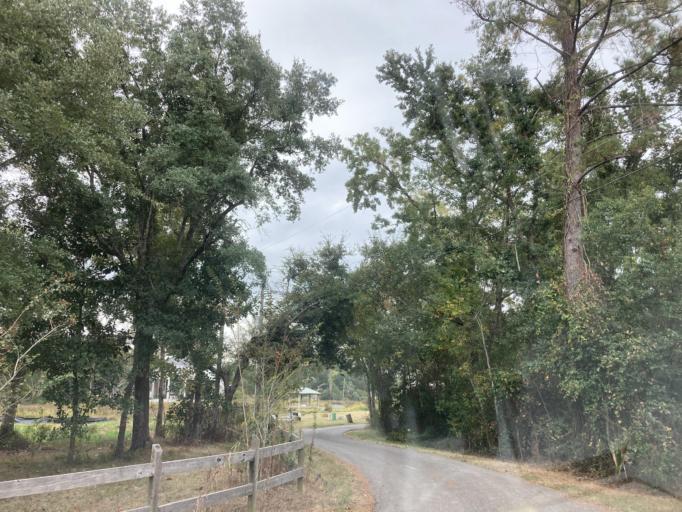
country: US
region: Mississippi
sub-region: Jackson County
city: Gulf Hills
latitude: 30.4306
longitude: -88.8468
